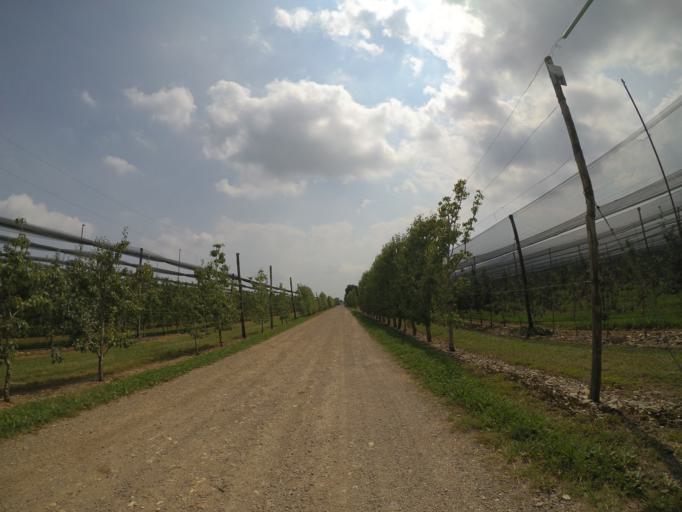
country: IT
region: Friuli Venezia Giulia
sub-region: Provincia di Udine
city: Sedegliano
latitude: 45.9949
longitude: 13.0108
